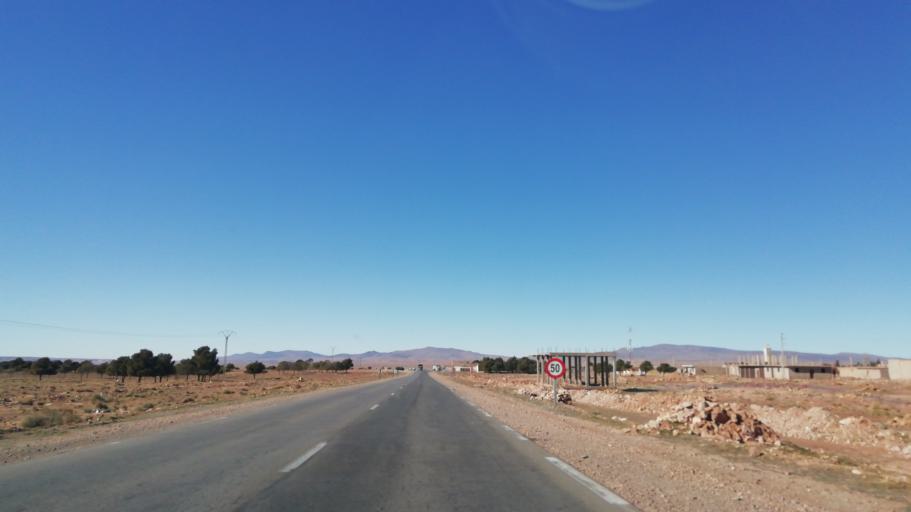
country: DZ
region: El Bayadh
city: El Bayadh
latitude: 33.6322
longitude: 1.3572
